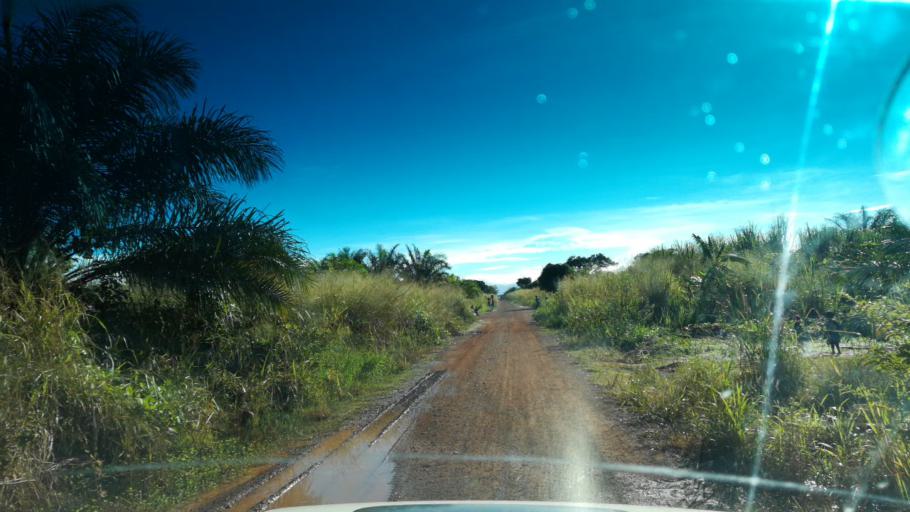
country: ZM
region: Northern
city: Kaputa
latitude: -8.3664
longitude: 28.9721
